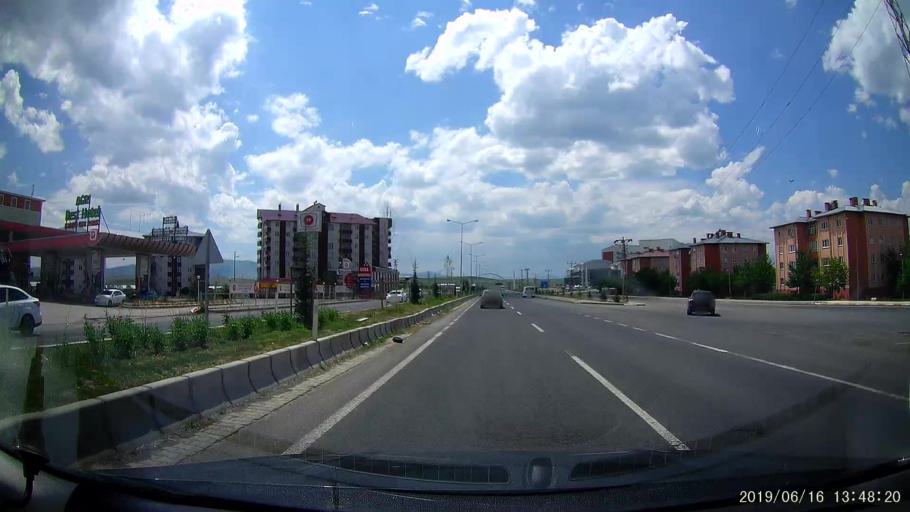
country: TR
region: Agri
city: Agri
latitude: 39.7144
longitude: 43.0088
